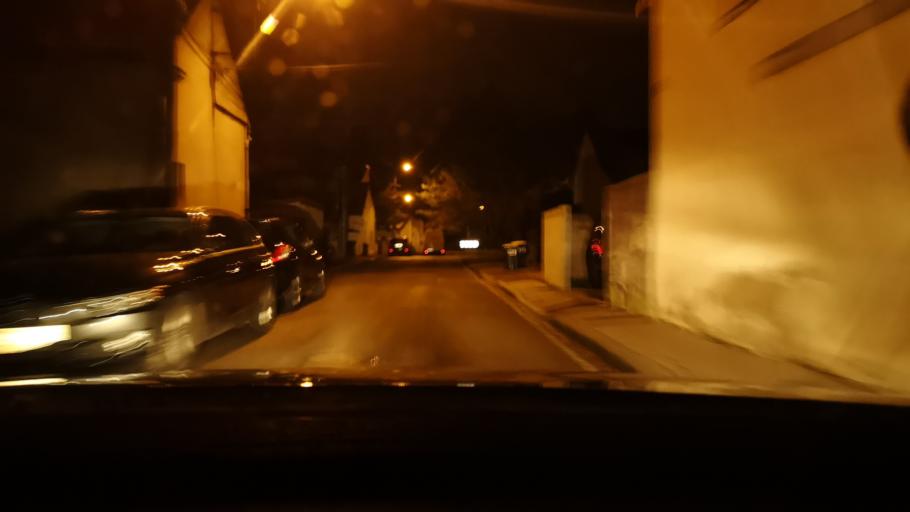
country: FR
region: Bourgogne
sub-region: Departement de Saone-et-Loire
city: Chalon-sur-Saone
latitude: 46.7929
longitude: 4.8604
